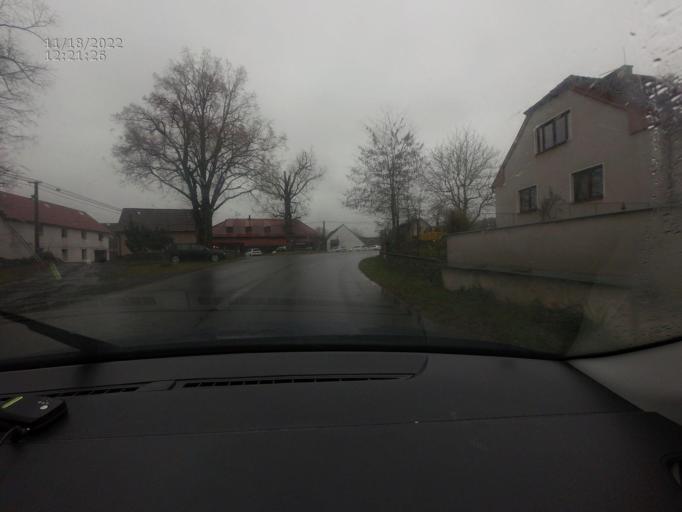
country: CZ
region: Plzensky
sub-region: Okres Plzen-Jih
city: Nepomuk
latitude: 49.4633
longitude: 13.5506
